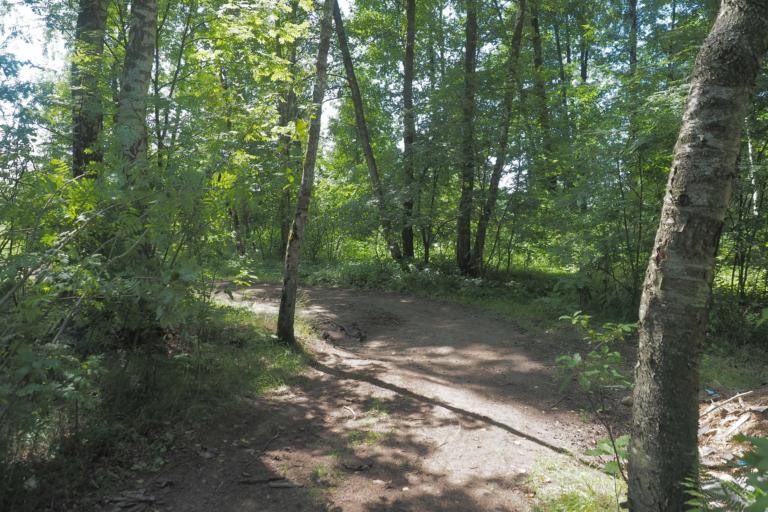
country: RU
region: Moskovskaya
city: Malyshevo
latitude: 55.5230
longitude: 38.3574
